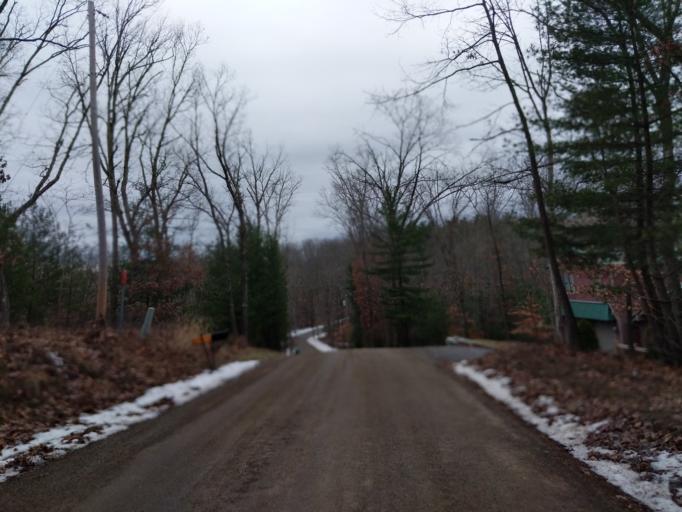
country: US
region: Ohio
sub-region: Athens County
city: The Plains
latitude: 39.3272
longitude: -82.1492
